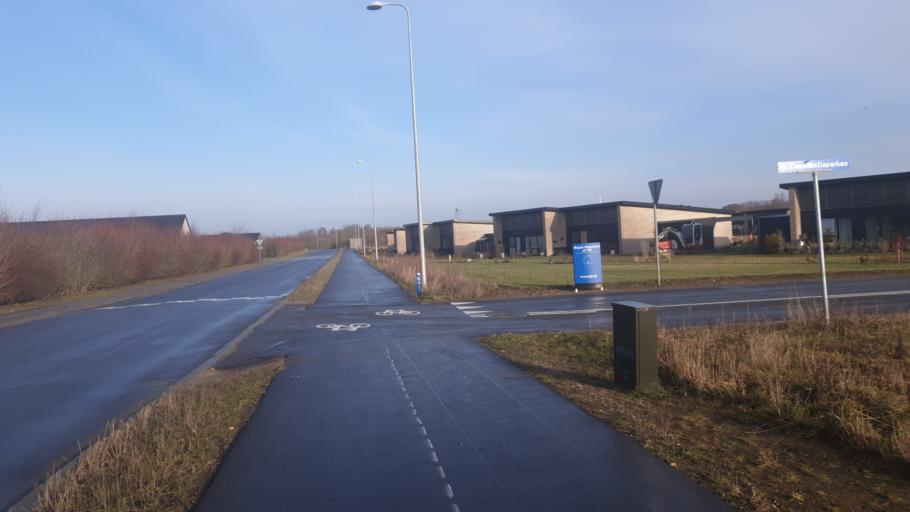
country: DK
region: Central Jutland
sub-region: Hedensted Kommune
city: Hedensted
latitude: 55.7640
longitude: 9.7240
